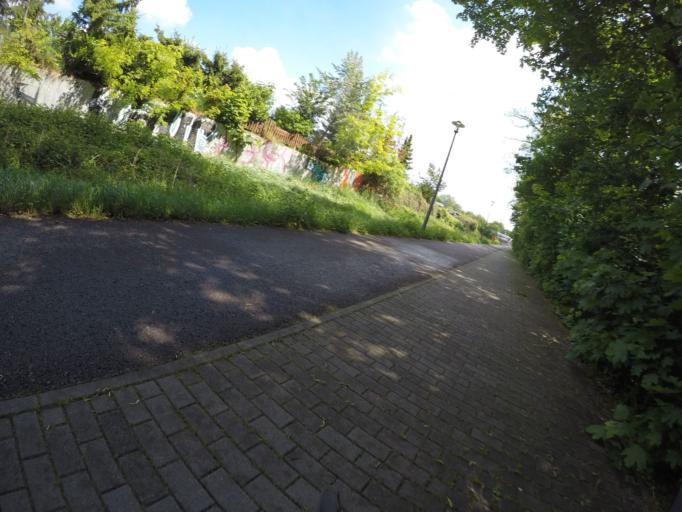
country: DE
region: Berlin
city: Biesdorf
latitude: 52.5132
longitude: 13.5595
